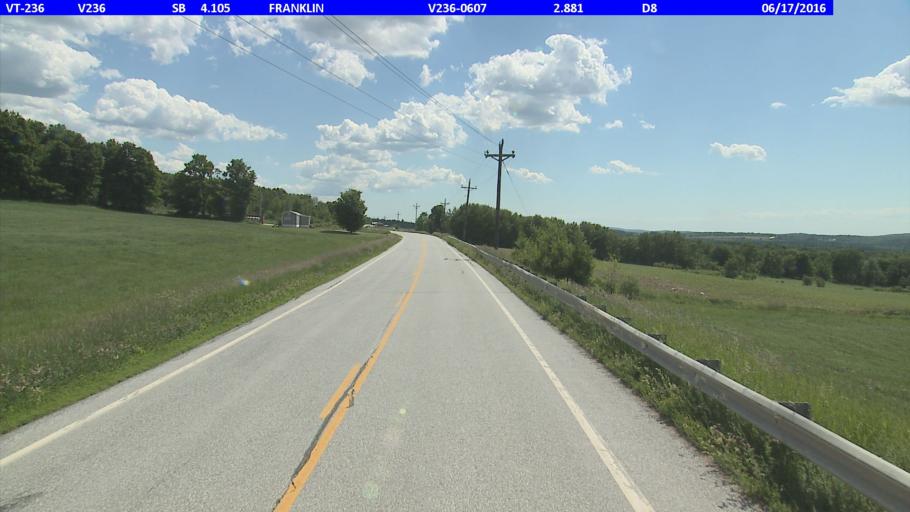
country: US
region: Vermont
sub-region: Franklin County
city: Enosburg Falls
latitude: 44.9685
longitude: -72.8543
